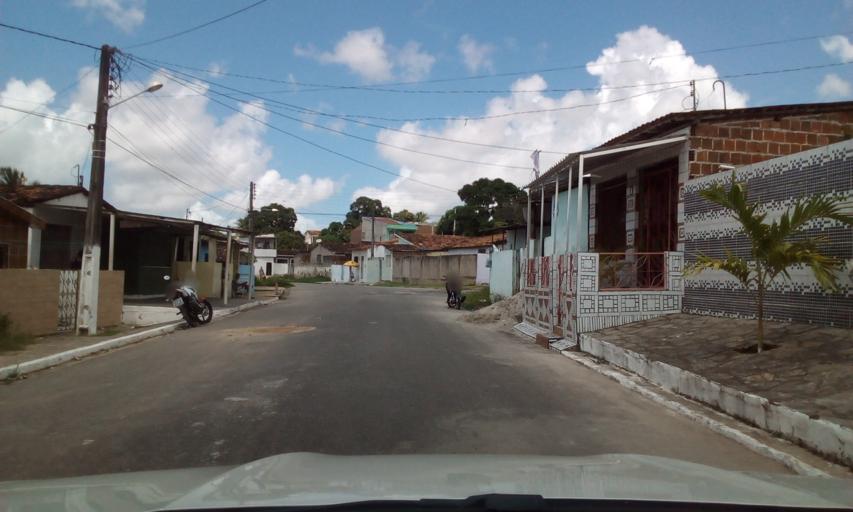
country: BR
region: Paraiba
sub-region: Bayeux
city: Bayeux
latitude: -7.1321
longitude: -34.9253
